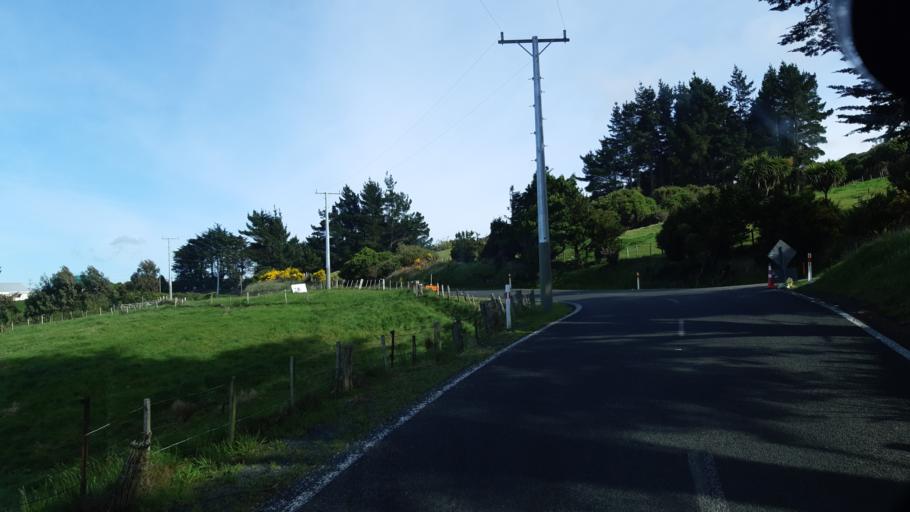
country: NZ
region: Otago
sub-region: Dunedin City
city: Portobello
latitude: -45.8772
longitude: 170.6276
